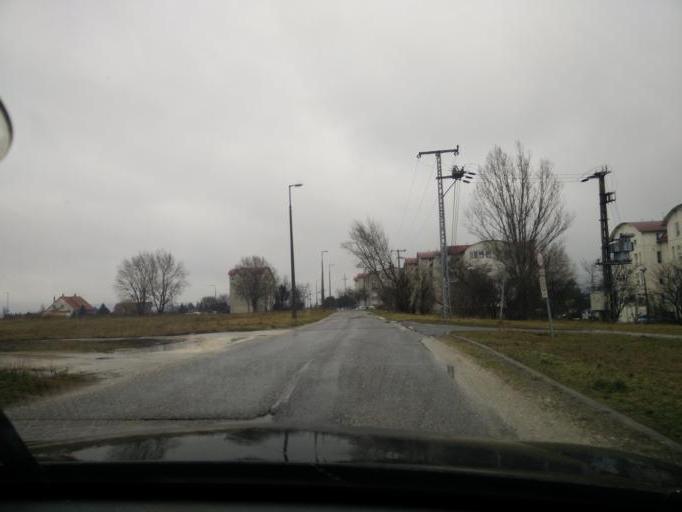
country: HU
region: Pest
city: Pilisszentivan
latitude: 47.6110
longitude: 18.9011
